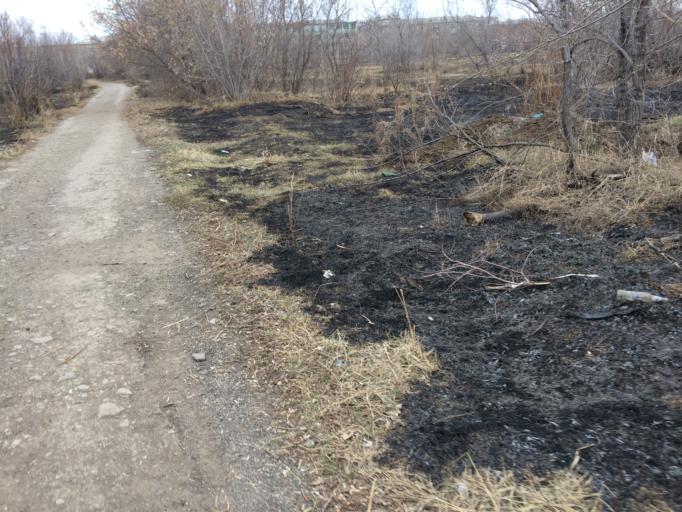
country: RU
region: Chelyabinsk
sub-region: Gorod Magnitogorsk
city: Magnitogorsk
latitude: 53.4403
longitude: 58.9768
